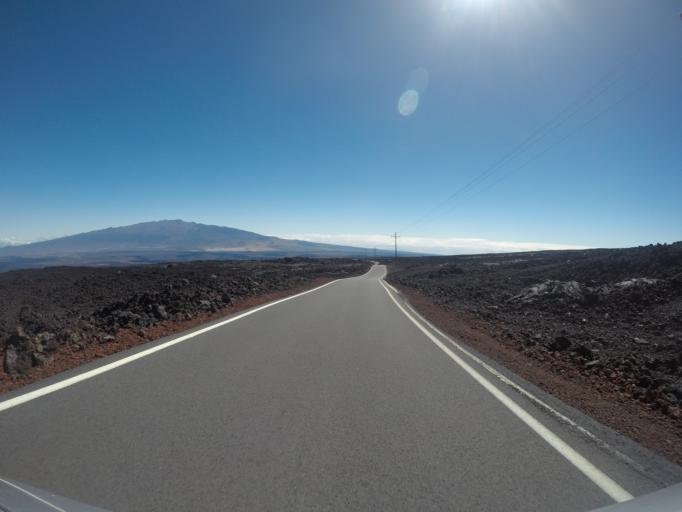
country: US
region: Hawaii
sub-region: Hawaii County
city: Volcano
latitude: 19.5557
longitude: -155.5356
